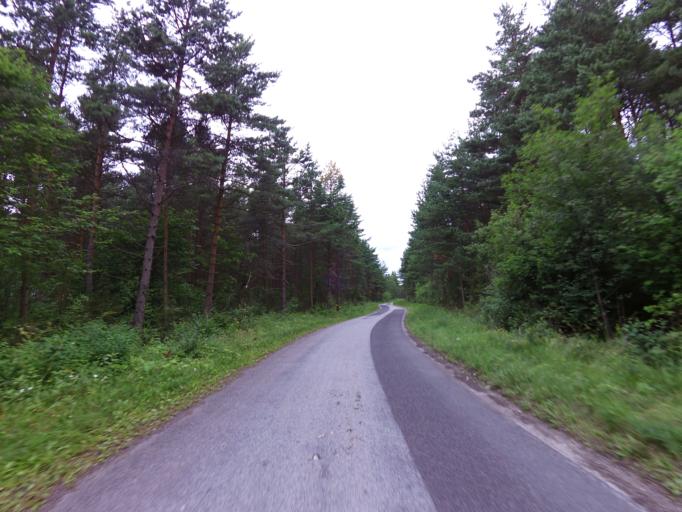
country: EE
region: Laeaene
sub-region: Vormsi vald
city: Hullo
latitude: 58.9759
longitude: 23.2584
